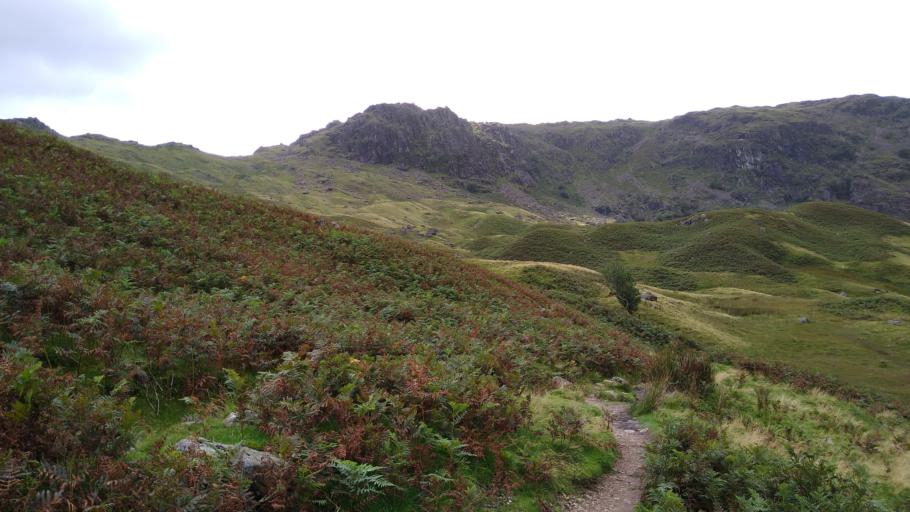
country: GB
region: England
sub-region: Cumbria
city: Ambleside
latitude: 54.4671
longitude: -3.0712
